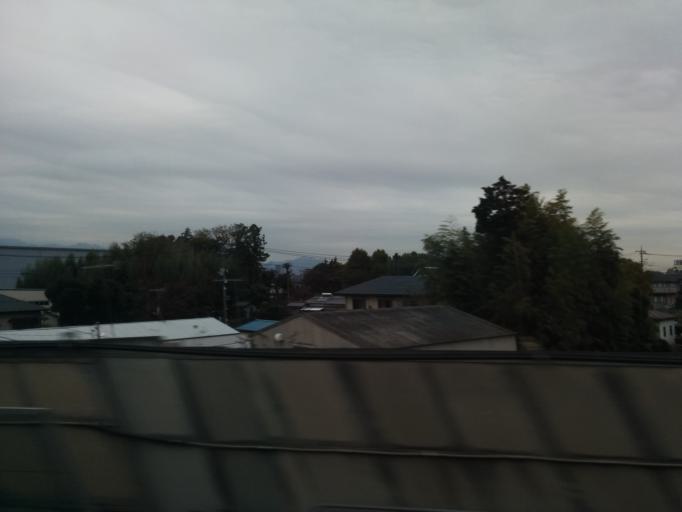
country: JP
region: Kanagawa
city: Atsugi
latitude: 35.3986
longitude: 139.3899
